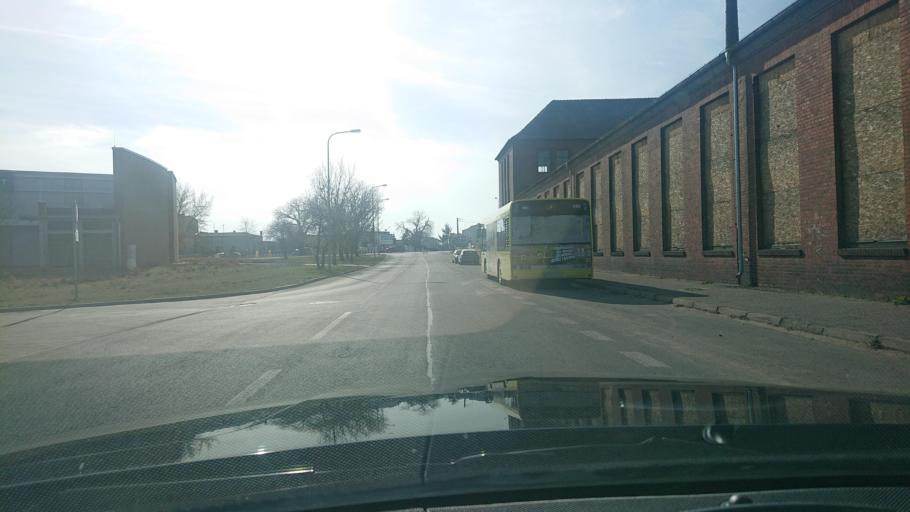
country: PL
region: Greater Poland Voivodeship
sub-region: Powiat gnieznienski
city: Gniezno
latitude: 52.5276
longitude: 17.5994
